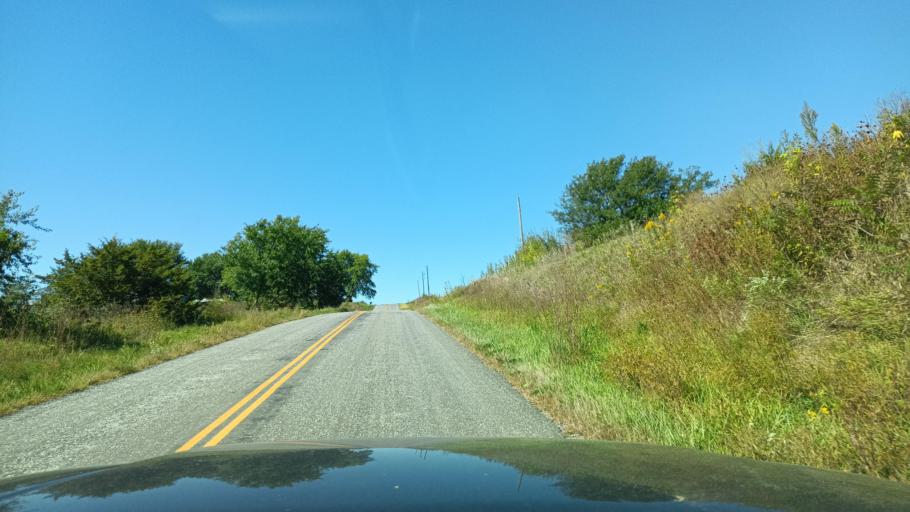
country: US
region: Missouri
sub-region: Adair County
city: Kirksville
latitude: 40.3304
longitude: -92.5214
